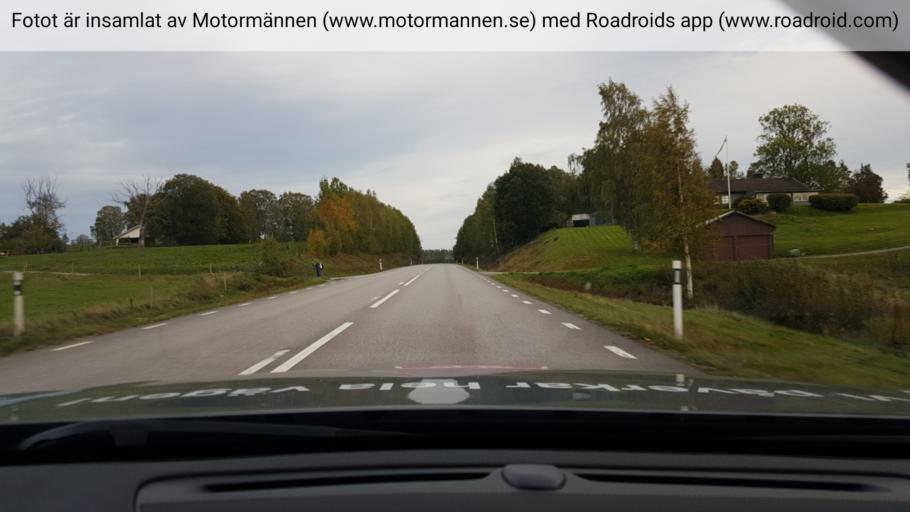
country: SE
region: Vaestra Goetaland
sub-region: Bengtsfors Kommun
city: Billingsfors
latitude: 59.0340
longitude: 12.3315
